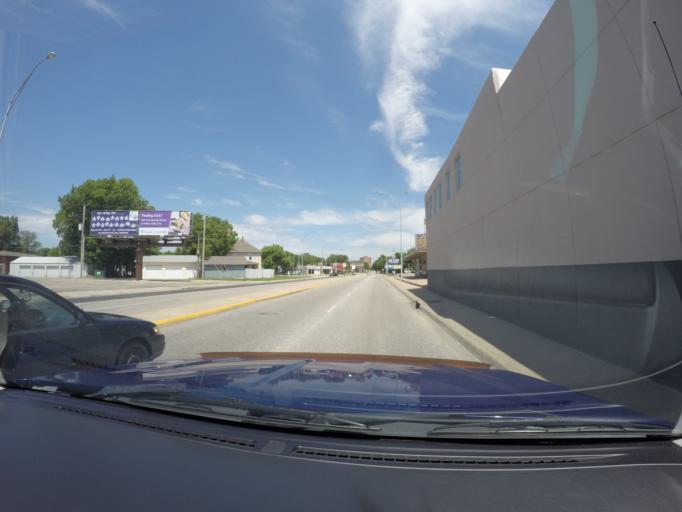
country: US
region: Nebraska
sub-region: Hall County
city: Grand Island
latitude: 40.9170
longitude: -98.3398
